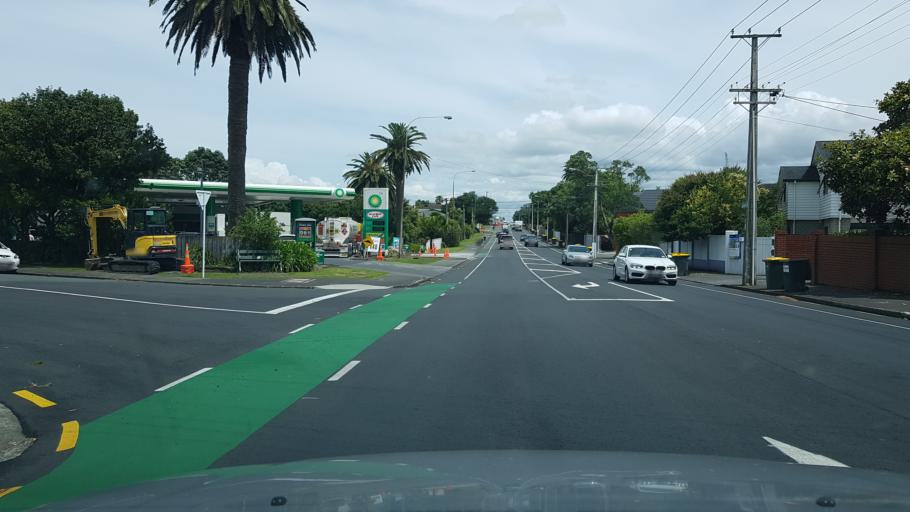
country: NZ
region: Auckland
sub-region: Auckland
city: North Shore
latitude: -36.7981
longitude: 174.7842
